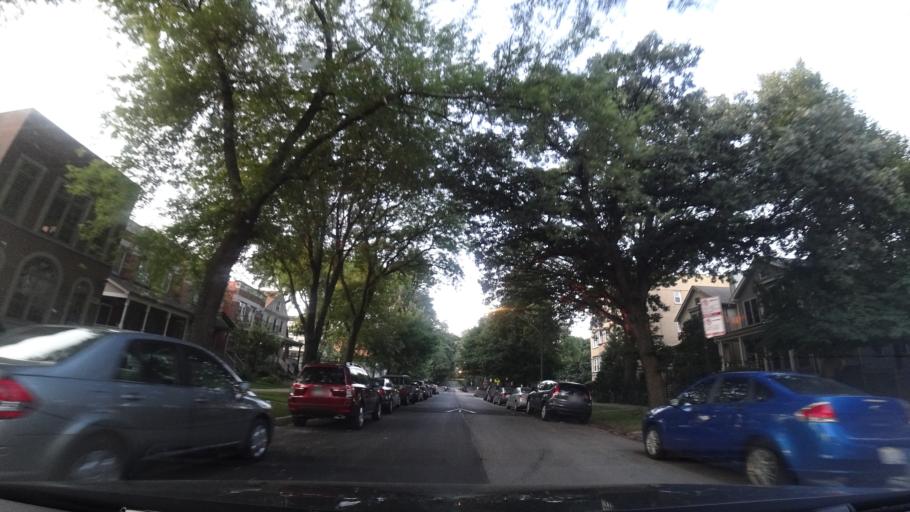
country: US
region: Illinois
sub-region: Cook County
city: Lincolnwood
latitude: 41.9677
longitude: -87.6762
